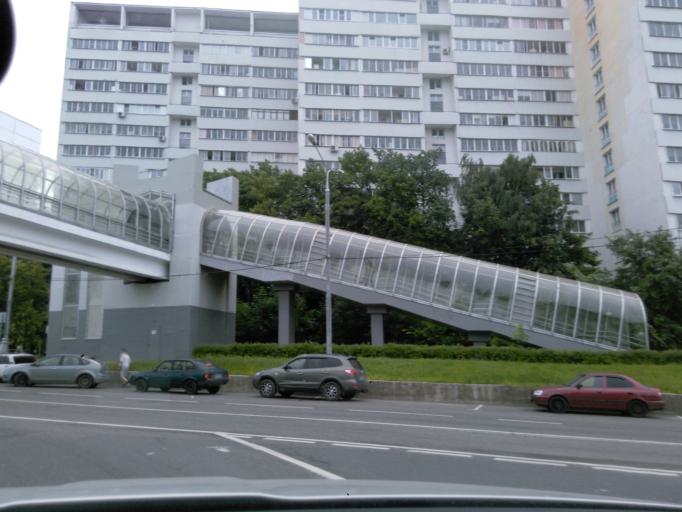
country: RU
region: Moskovskaya
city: Rzhavki
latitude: 55.9899
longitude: 37.2244
